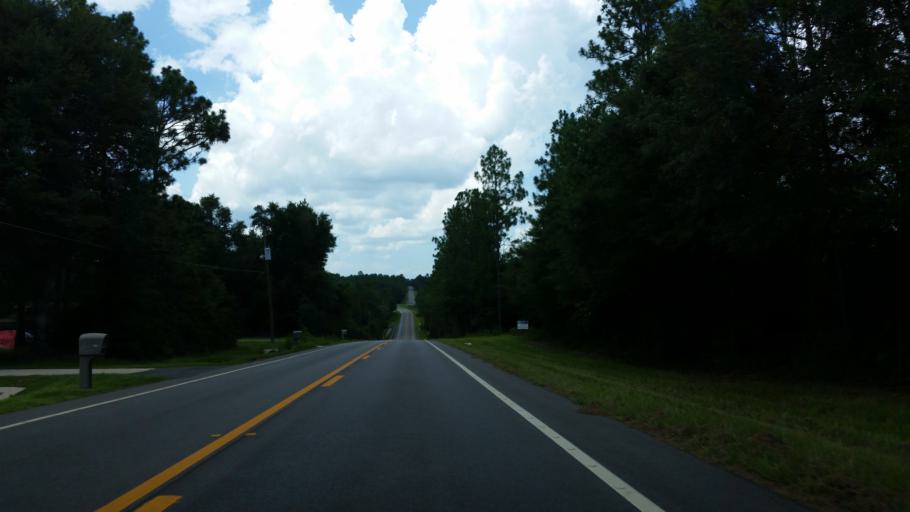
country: US
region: Florida
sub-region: Escambia County
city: Cantonment
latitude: 30.6532
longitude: -87.3856
